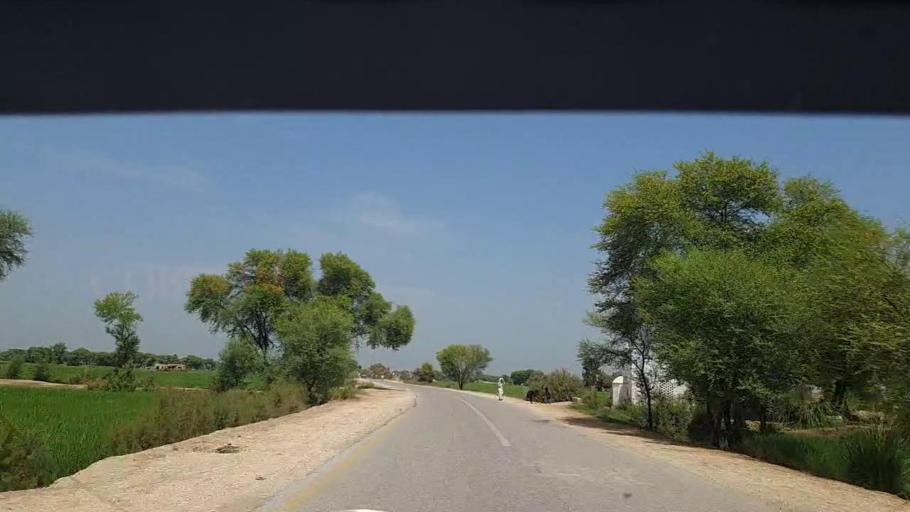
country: PK
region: Sindh
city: Thul
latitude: 28.1424
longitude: 68.8178
